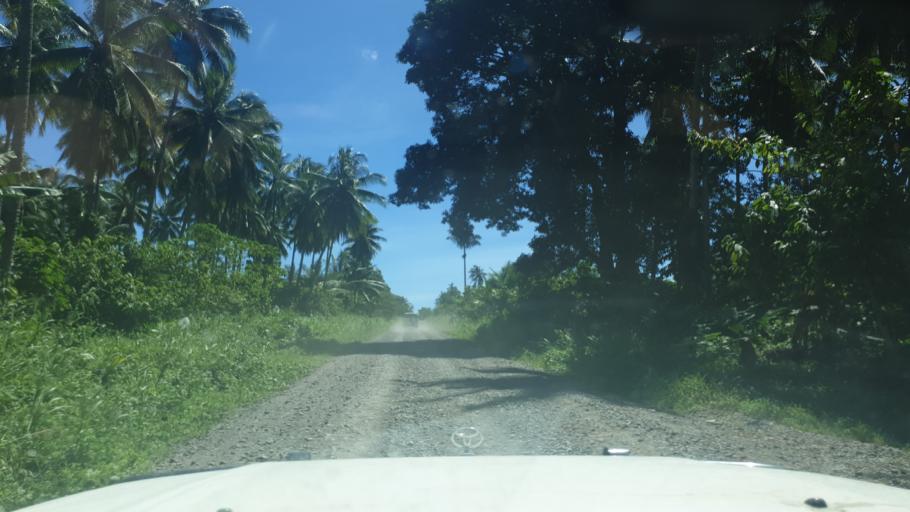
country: PG
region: Bougainville
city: Buka
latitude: -5.6660
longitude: 155.1001
